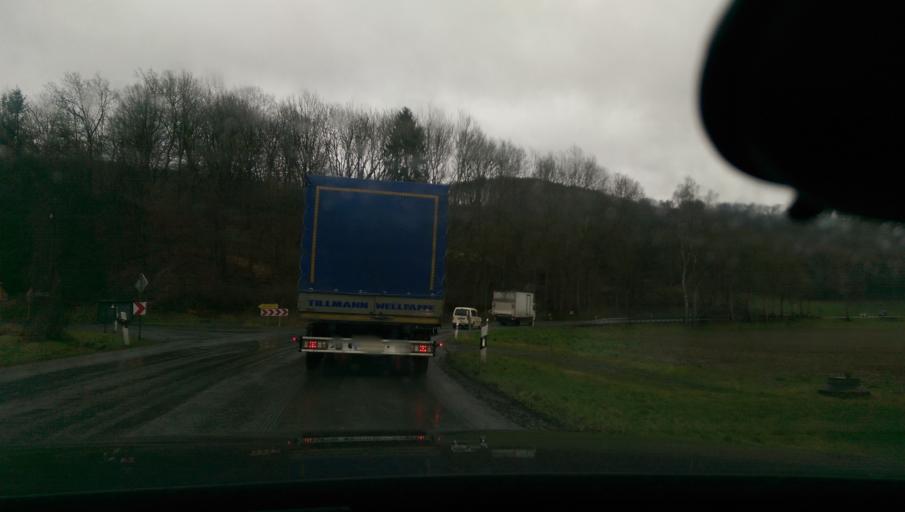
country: DE
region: North Rhine-Westphalia
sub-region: Regierungsbezirk Arnsberg
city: Sundern
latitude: 51.3971
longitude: 8.0056
